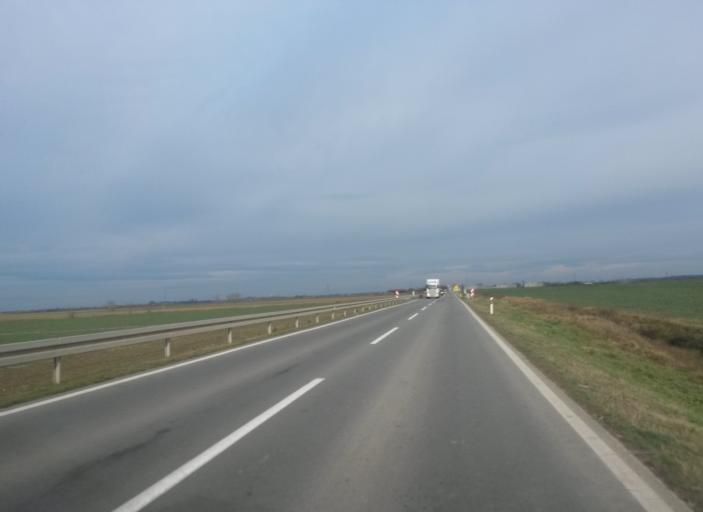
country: HR
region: Osjecko-Baranjska
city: Ovcara
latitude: 45.4844
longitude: 18.5443
